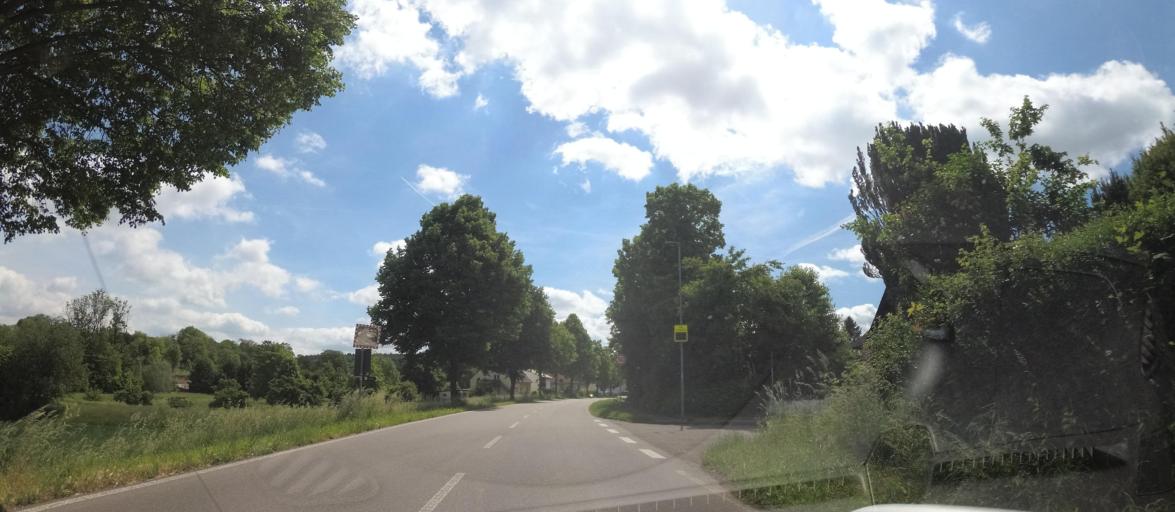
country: DE
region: Baden-Wuerttemberg
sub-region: Karlsruhe Region
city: Bretten
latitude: 49.0760
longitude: 8.7048
